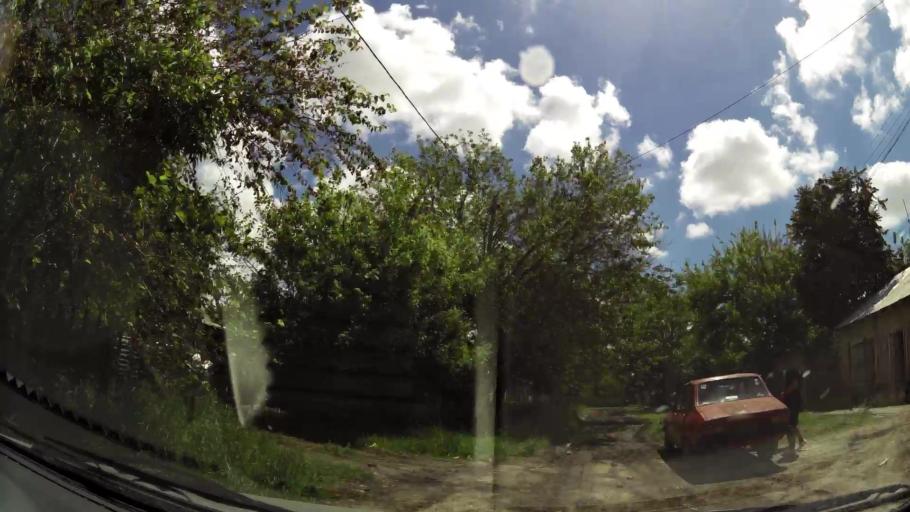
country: AR
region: Buenos Aires
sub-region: Partido de Quilmes
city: Quilmes
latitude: -34.8135
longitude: -58.2364
